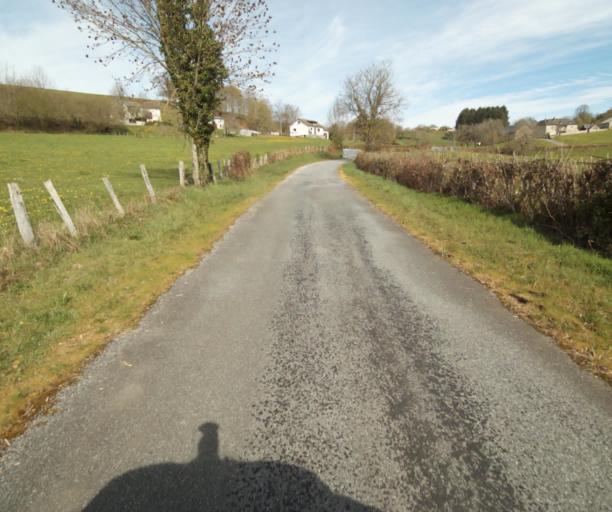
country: FR
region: Limousin
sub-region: Departement de la Correze
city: Laguenne
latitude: 45.2660
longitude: 1.8134
